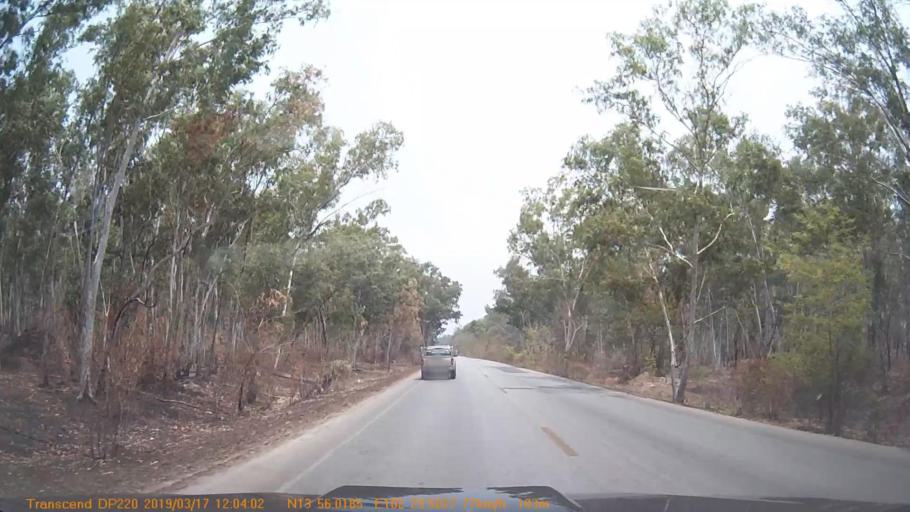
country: TH
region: Sa Kaeo
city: Khok Sung
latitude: 13.9339
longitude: 102.4919
